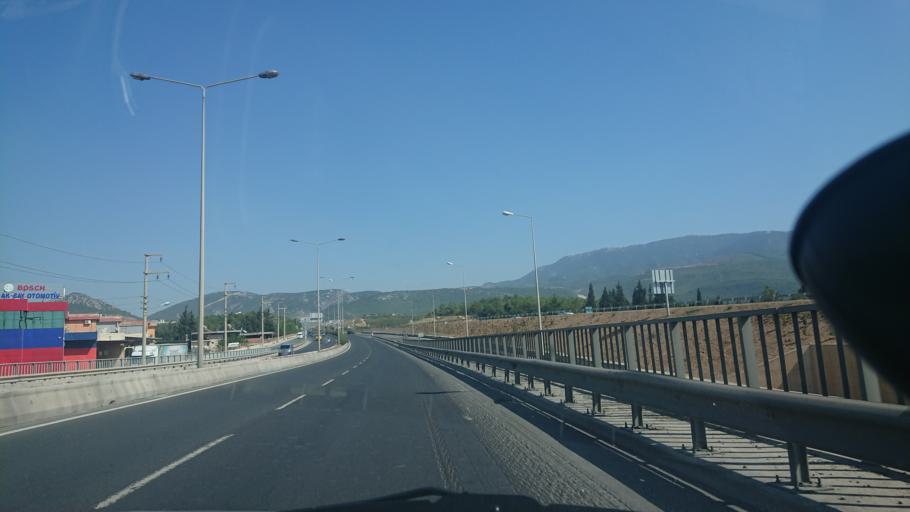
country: TR
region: Izmir
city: Bornova
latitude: 38.4518
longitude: 27.2678
